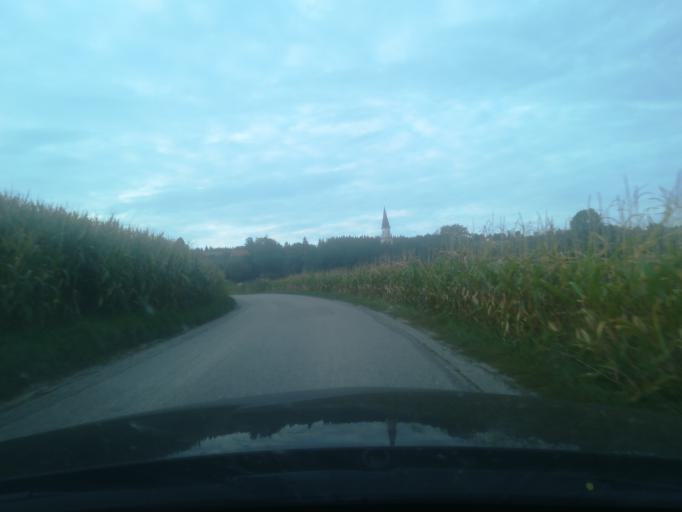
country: AT
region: Upper Austria
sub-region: Wels-Land
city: Buchkirchen
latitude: 48.2520
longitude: 14.0487
